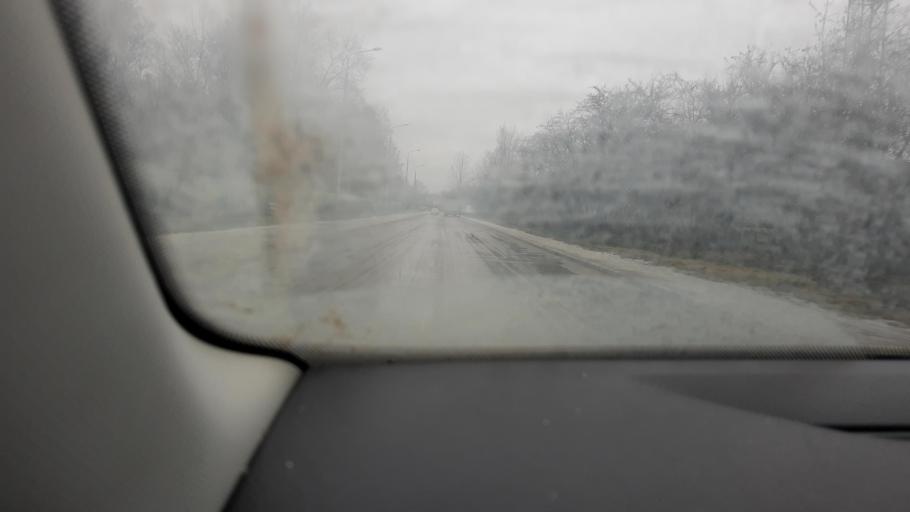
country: RU
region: Moscow
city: Tsaritsyno
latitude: 55.6243
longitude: 37.6376
